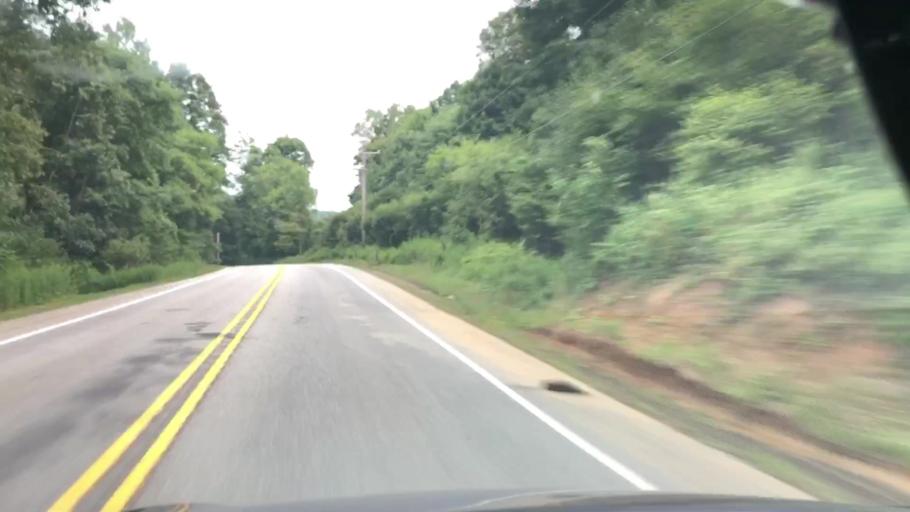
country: US
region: Pennsylvania
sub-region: Venango County
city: Hasson Heights
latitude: 41.5142
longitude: -79.7045
